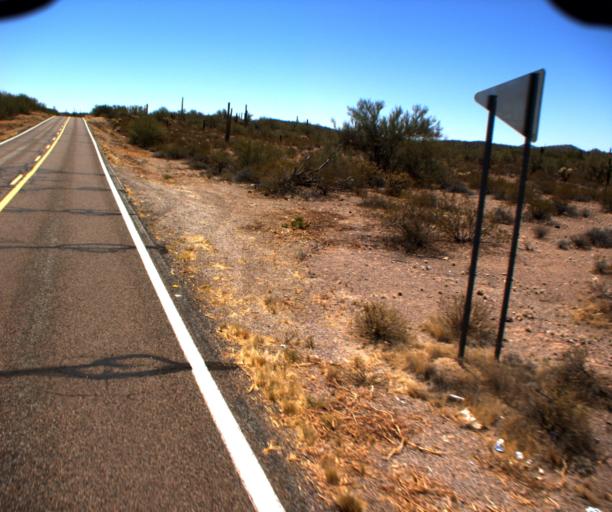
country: US
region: Arizona
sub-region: Pima County
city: Ajo
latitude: 32.2119
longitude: -112.6277
